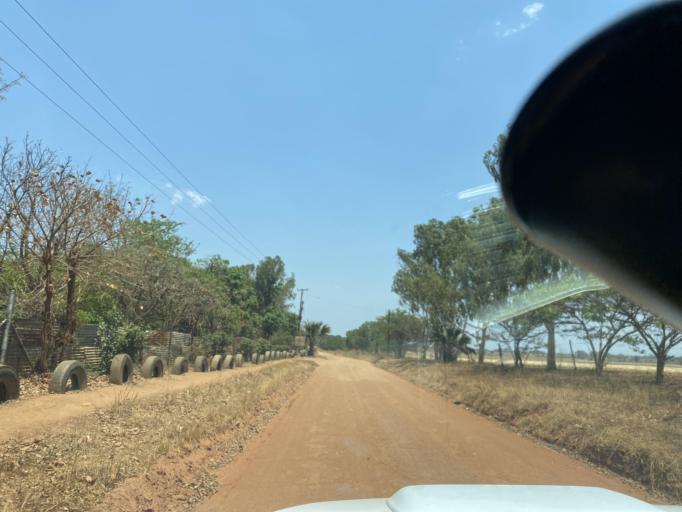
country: ZM
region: Lusaka
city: Lusaka
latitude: -15.4458
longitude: 28.0498
